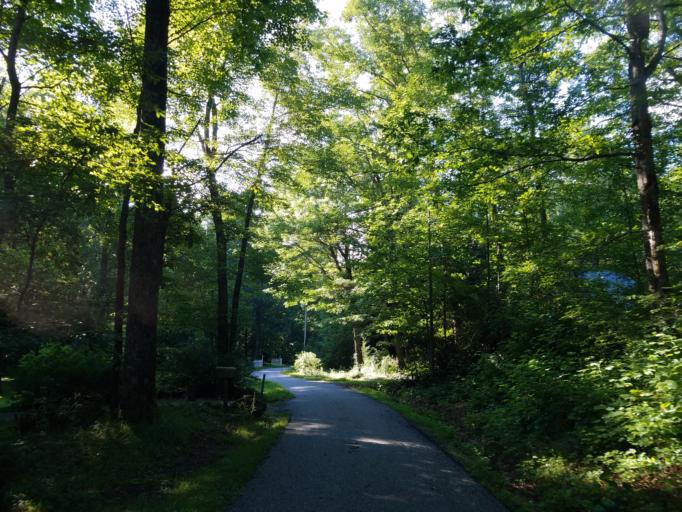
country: US
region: Georgia
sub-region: Lumpkin County
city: Dahlonega
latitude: 34.6768
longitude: -84.0144
